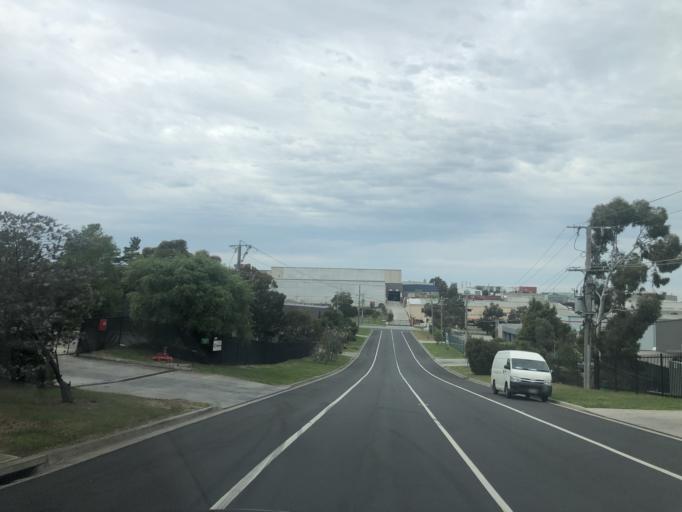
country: AU
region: Victoria
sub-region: Casey
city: Hallam
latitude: -38.0119
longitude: 145.2645
